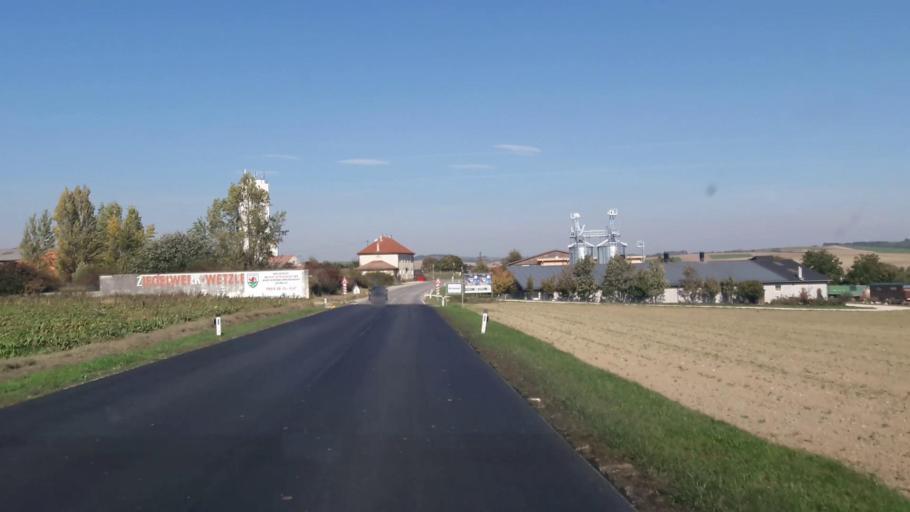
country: AT
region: Lower Austria
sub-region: Politischer Bezirk Korneuburg
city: Grossrussbach
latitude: 48.4722
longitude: 16.3800
